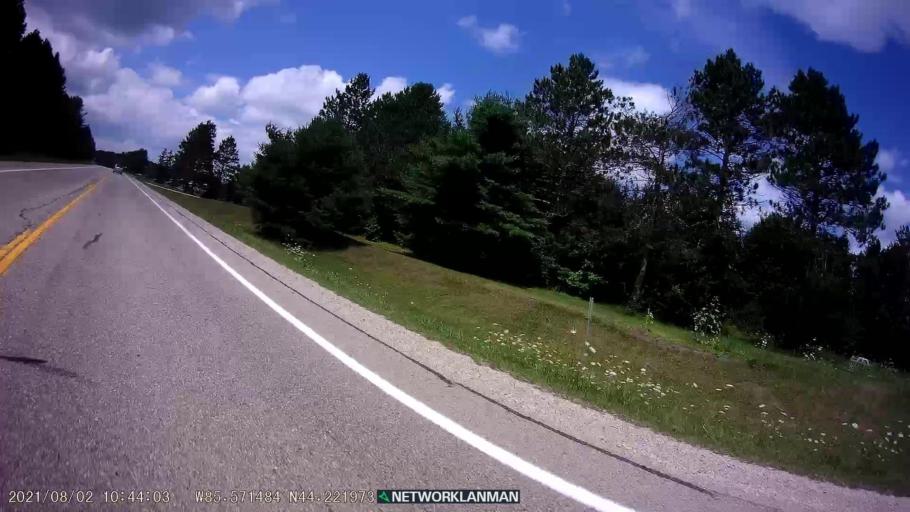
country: US
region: Michigan
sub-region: Wexford County
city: Cadillac
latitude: 44.2220
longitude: -85.5720
